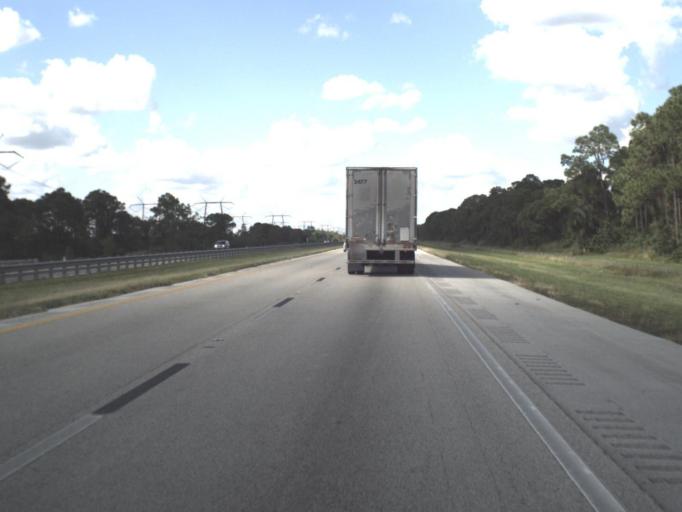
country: US
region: Florida
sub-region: Indian River County
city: West Vero Corridor
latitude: 27.5347
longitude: -80.6110
